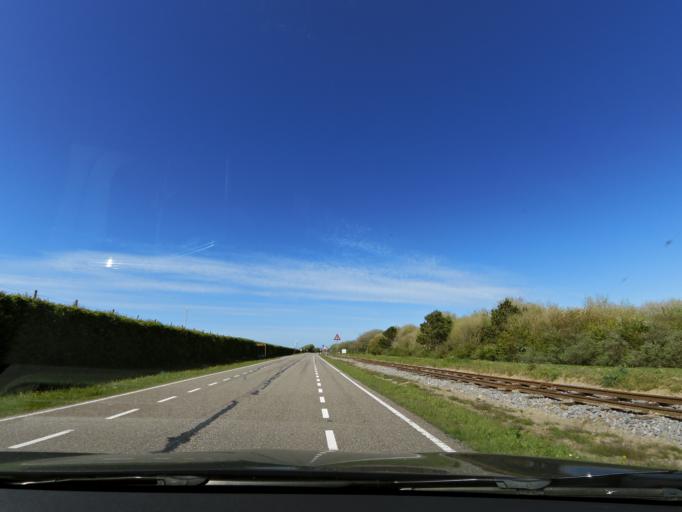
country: NL
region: Zeeland
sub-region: Schouwen-Duiveland
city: Scharendijke
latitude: 51.7818
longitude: 3.8692
